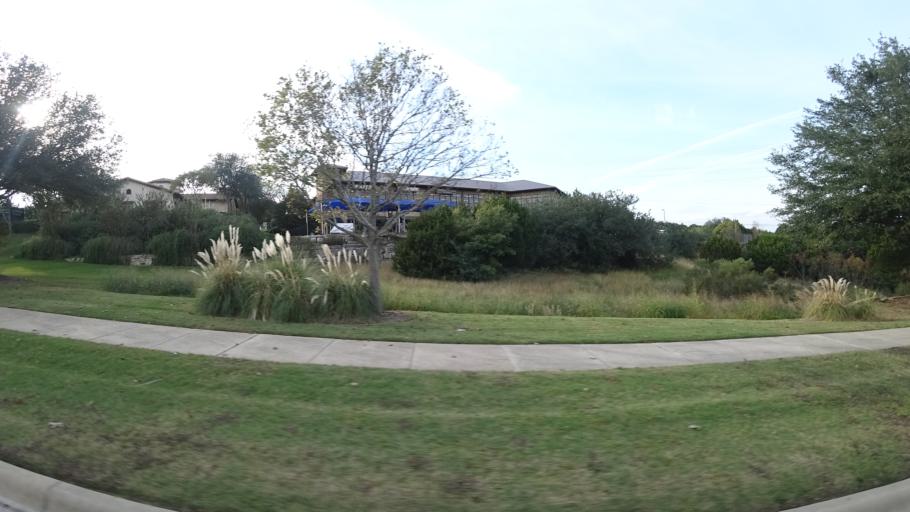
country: US
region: Texas
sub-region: Travis County
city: Hudson Bend
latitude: 30.3831
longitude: -97.8837
